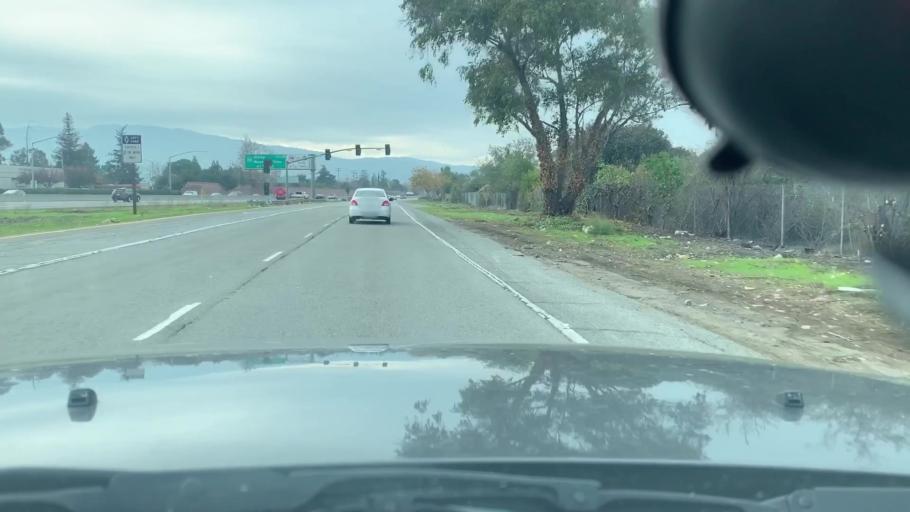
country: US
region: California
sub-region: Santa Clara County
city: Campbell
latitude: 37.2688
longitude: -121.9483
